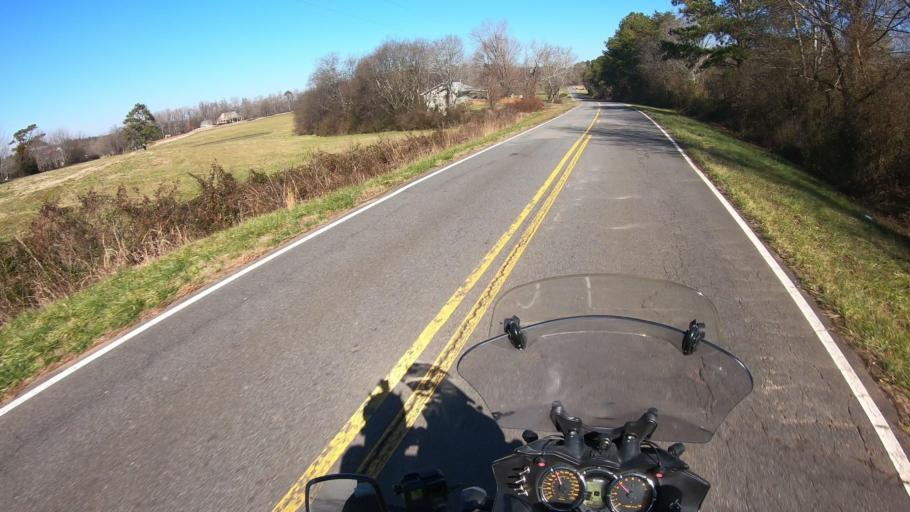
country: US
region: Georgia
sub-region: Bartow County
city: Rydal
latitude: 34.3244
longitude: -84.7576
